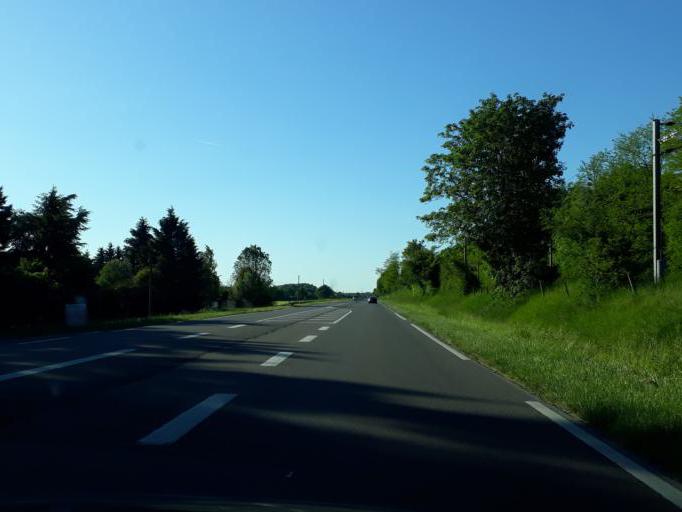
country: FR
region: Bourgogne
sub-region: Departement de la Nievre
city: Neuvy-sur-Loire
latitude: 47.5337
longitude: 2.8646
